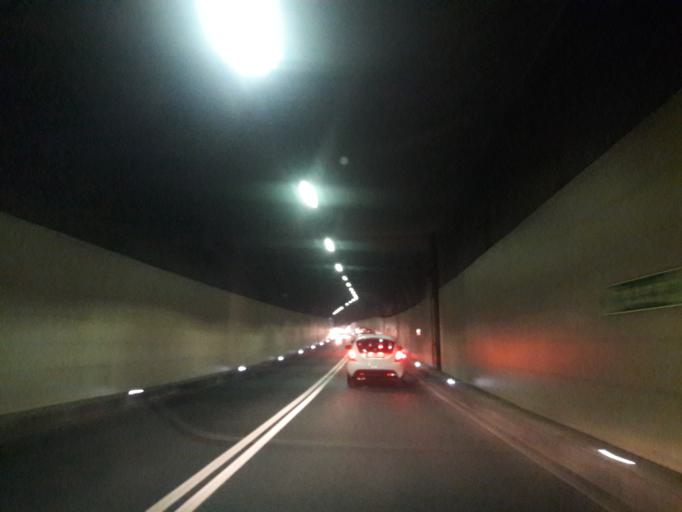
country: PT
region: Madeira
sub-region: Funchal
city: Nossa Senhora do Monte
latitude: 32.6502
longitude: -16.9162
